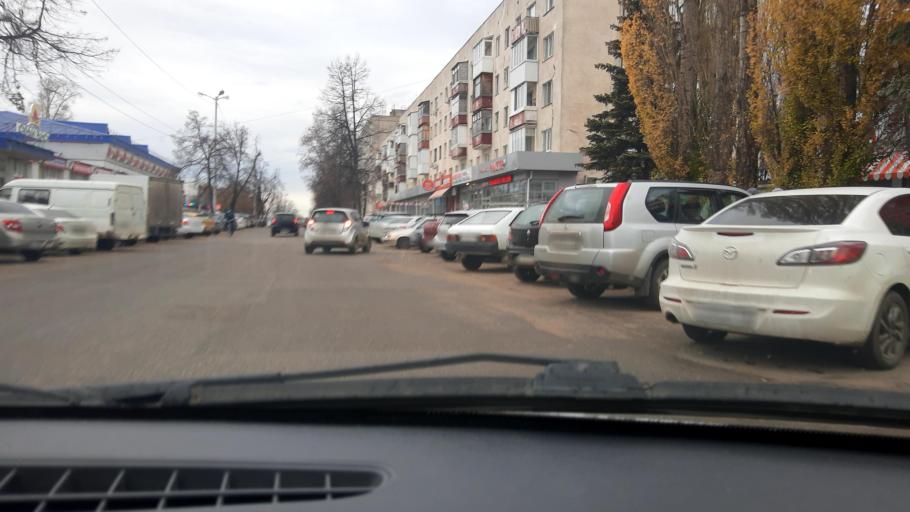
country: RU
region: Bashkortostan
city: Mikhaylovka
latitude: 54.7069
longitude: 55.8287
